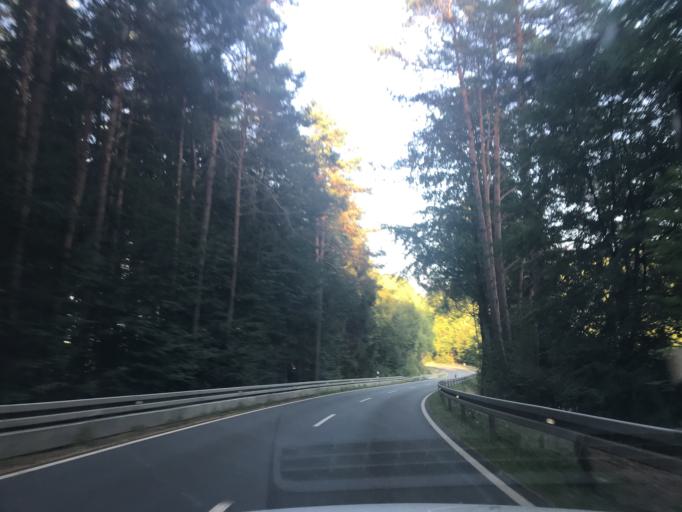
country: DE
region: Bavaria
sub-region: Upper Franconia
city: Pottenstein
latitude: 49.7120
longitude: 11.4292
